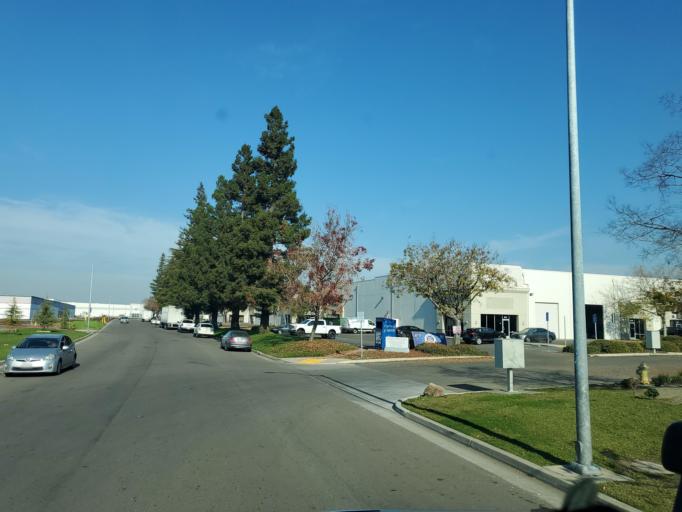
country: US
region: California
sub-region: San Joaquin County
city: Kennedy
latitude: 37.9074
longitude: -121.2285
